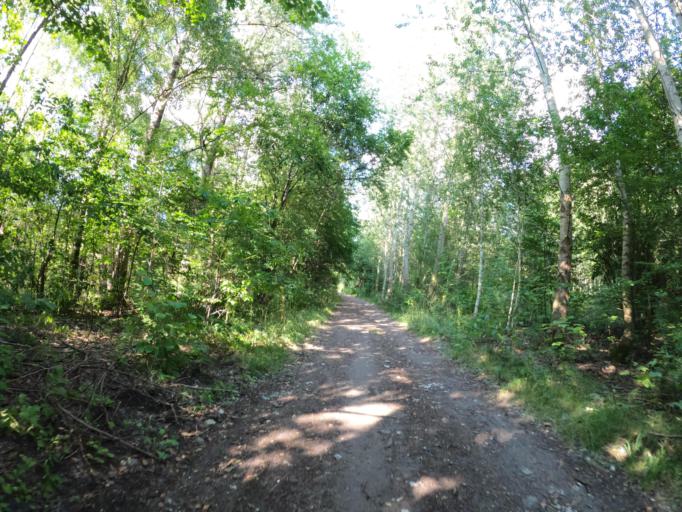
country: PL
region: West Pomeranian Voivodeship
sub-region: Koszalin
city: Koszalin
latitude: 54.1740
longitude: 16.2266
